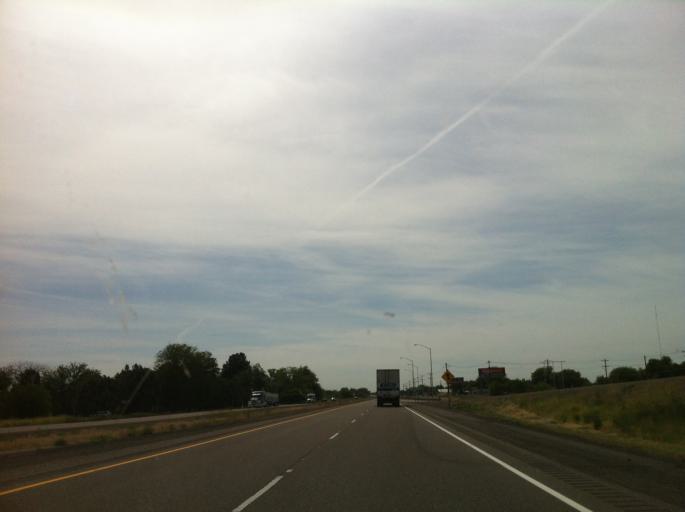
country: US
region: Oregon
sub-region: Malheur County
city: Ontario
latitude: 44.0509
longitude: -116.9795
